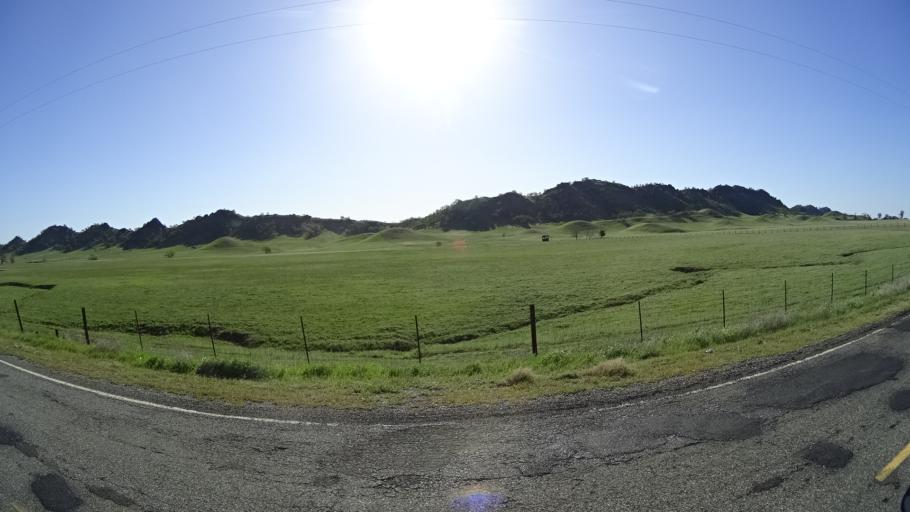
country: US
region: California
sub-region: Tehama County
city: Rancho Tehama Reserve
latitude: 39.7392
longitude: -122.5471
